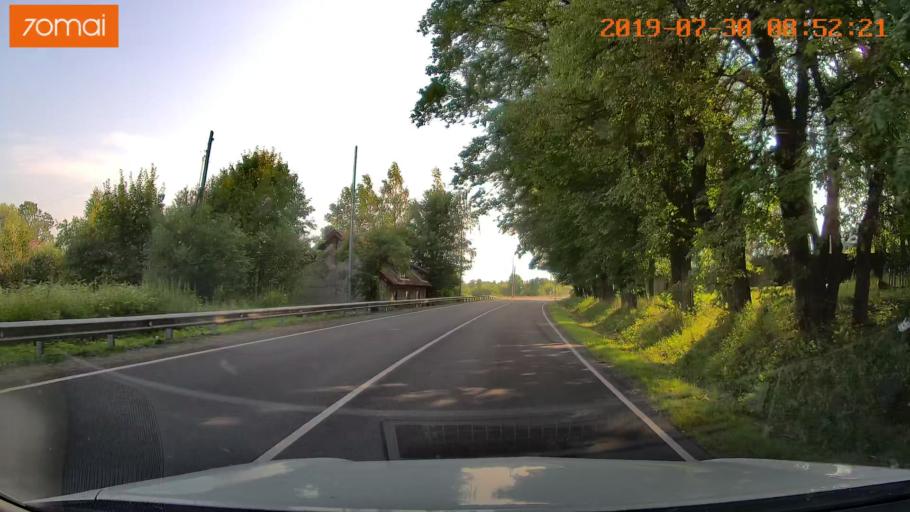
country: RU
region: Kaliningrad
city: Chernyakhovsk
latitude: 54.6021
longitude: 21.9720
